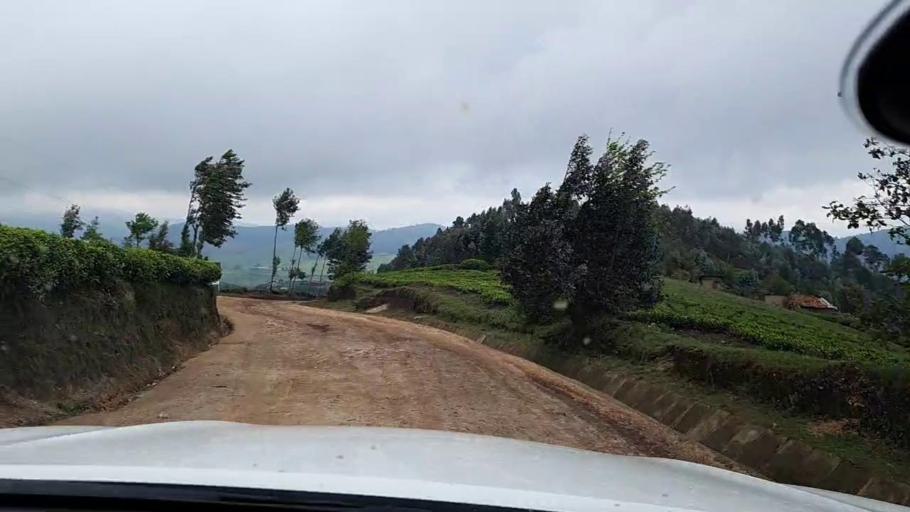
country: RW
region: Western Province
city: Kibuye
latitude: -2.2446
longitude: 29.3462
